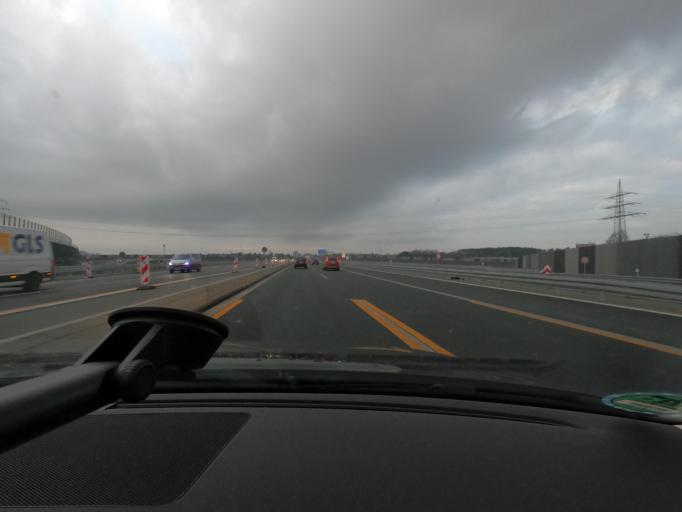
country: DE
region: Bavaria
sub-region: Regierungsbezirk Mittelfranken
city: Erlangen
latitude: 49.5567
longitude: 10.9924
